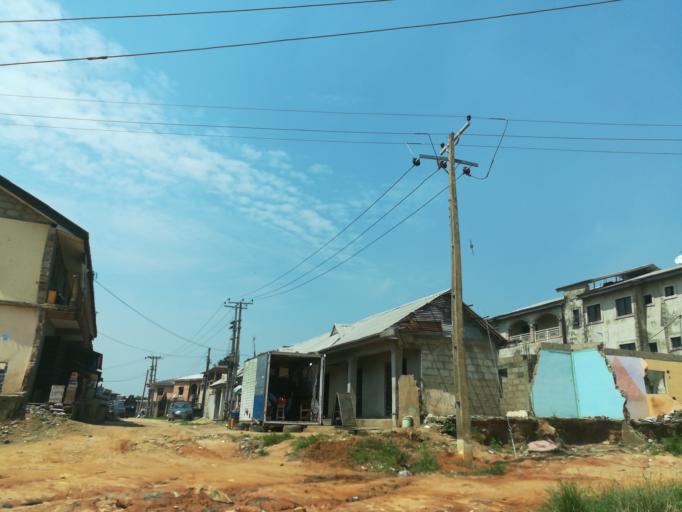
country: NG
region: Lagos
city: Ikorodu
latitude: 6.6591
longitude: 3.4731
